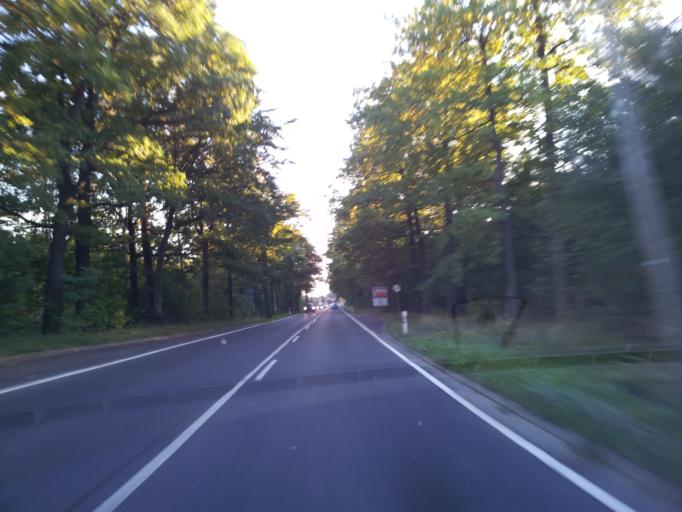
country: DE
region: Saxony
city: Ottendorf-Okrilla
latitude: 51.2064
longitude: 13.8381
